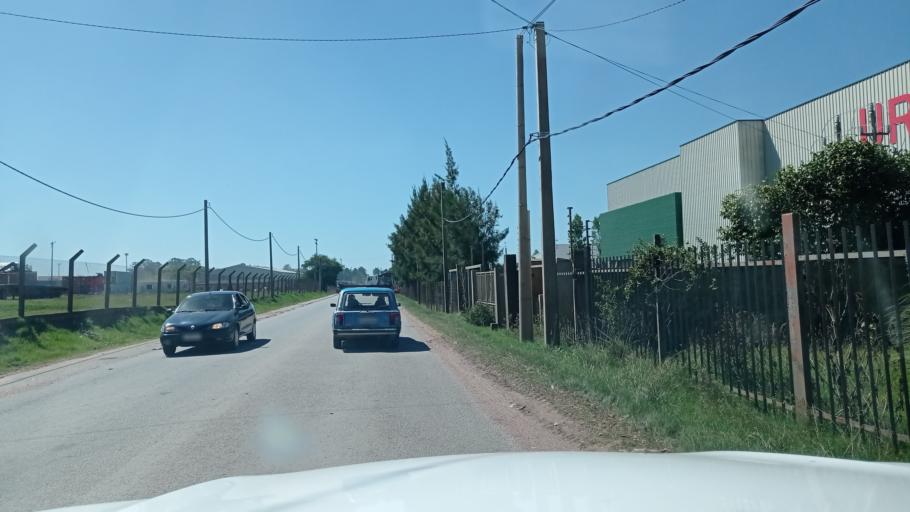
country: UY
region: Montevideo
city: Pajas Blancas
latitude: -34.8646
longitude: -56.2878
